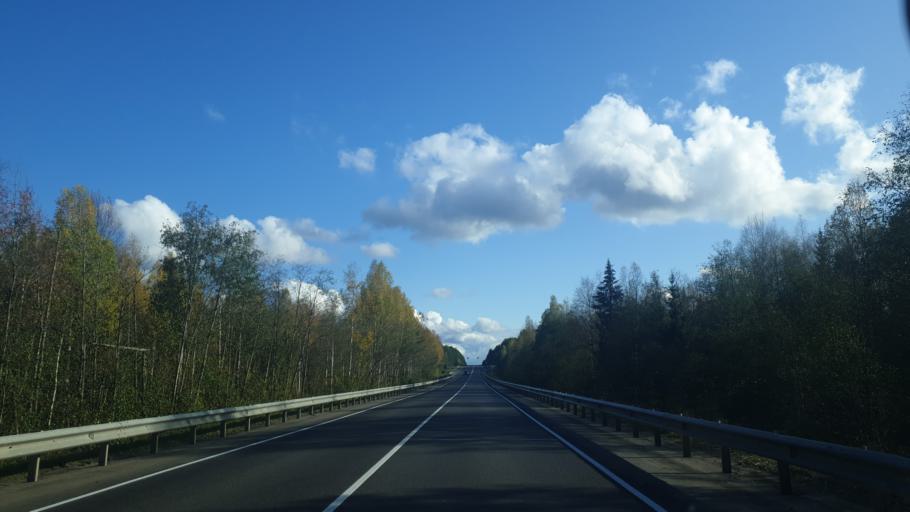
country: RU
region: Komi Republic
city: Letka
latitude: 60.2532
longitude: 49.6763
